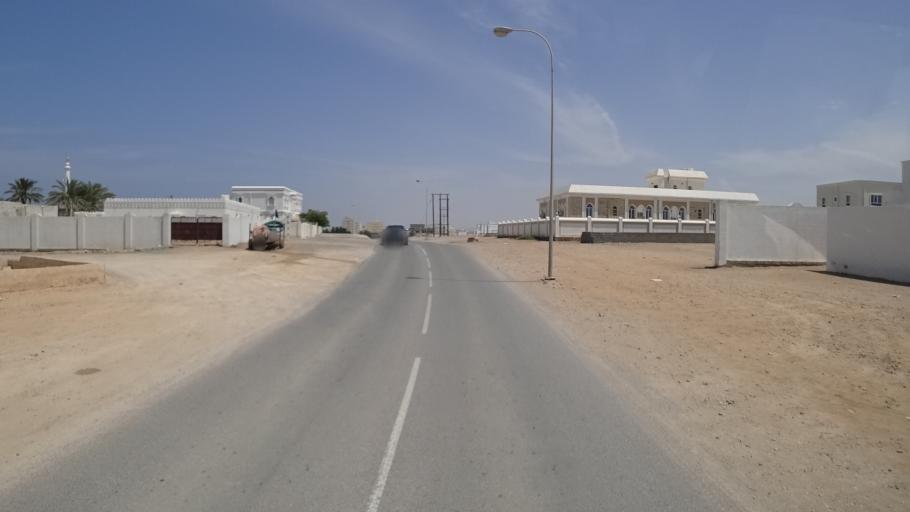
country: OM
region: Ash Sharqiyah
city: Sur
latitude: 22.6113
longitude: 59.4660
